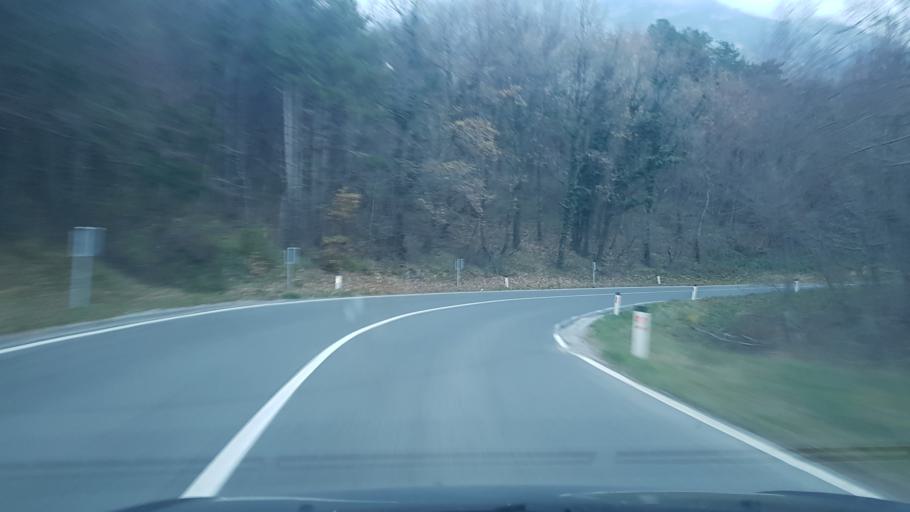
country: SI
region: Ajdovscina
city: Ajdovscina
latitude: 45.8841
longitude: 13.9362
